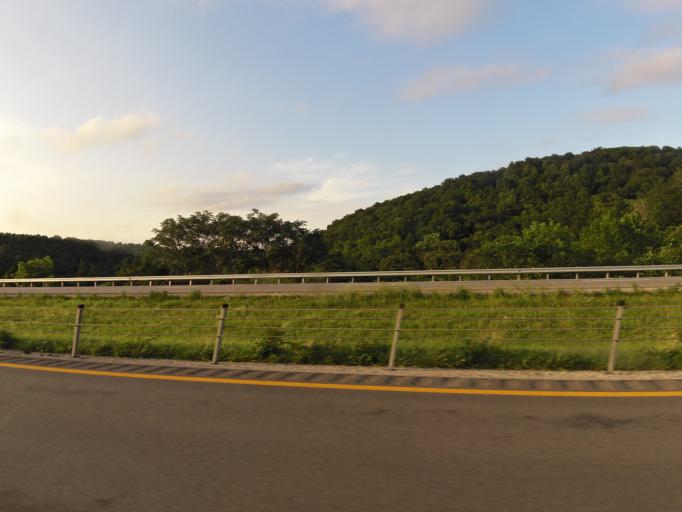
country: US
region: Kentucky
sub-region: Rockcastle County
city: Mount Vernon
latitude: 37.3707
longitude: -84.3188
